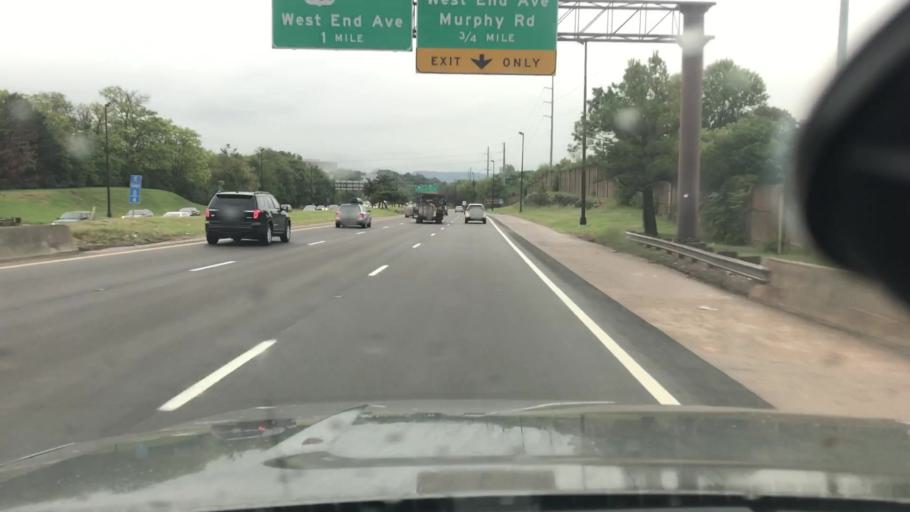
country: US
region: Tennessee
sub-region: Davidson County
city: Nashville
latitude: 36.1520
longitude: -86.8228
